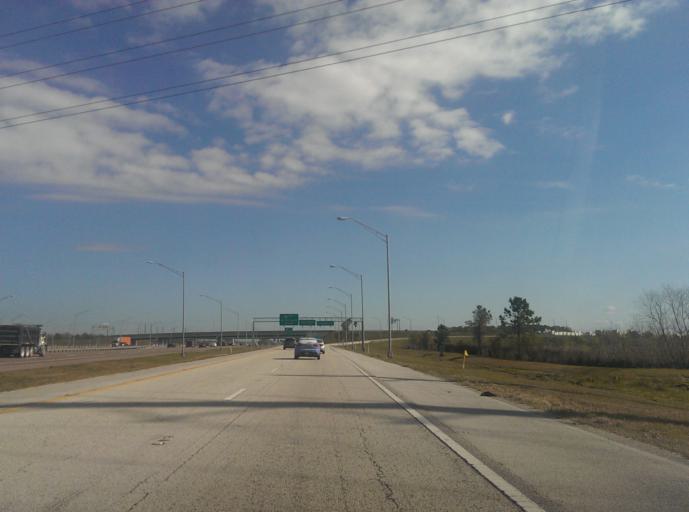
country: US
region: Florida
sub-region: Osceola County
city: Celebration
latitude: 28.3023
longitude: -81.5735
